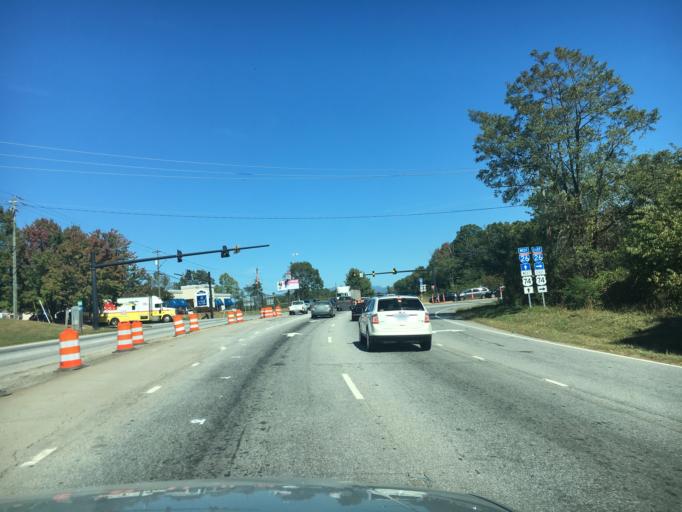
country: US
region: North Carolina
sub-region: Buncombe County
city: Bent Creek
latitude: 35.5328
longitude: -82.6045
